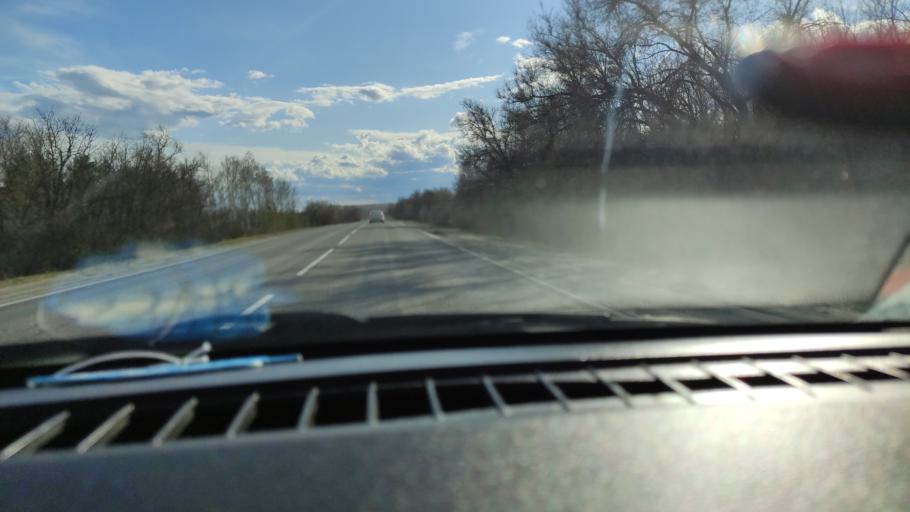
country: RU
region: Saratov
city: Sennoy
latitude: 52.1123
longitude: 46.8319
